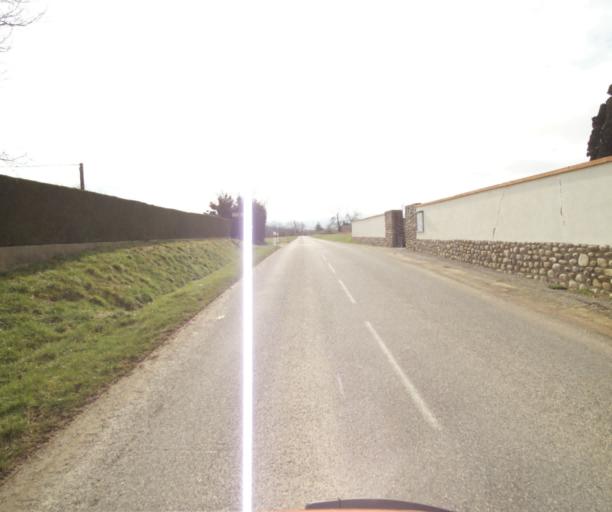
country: FR
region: Midi-Pyrenees
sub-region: Departement de l'Ariege
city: Pamiers
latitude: 43.1217
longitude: 1.5483
